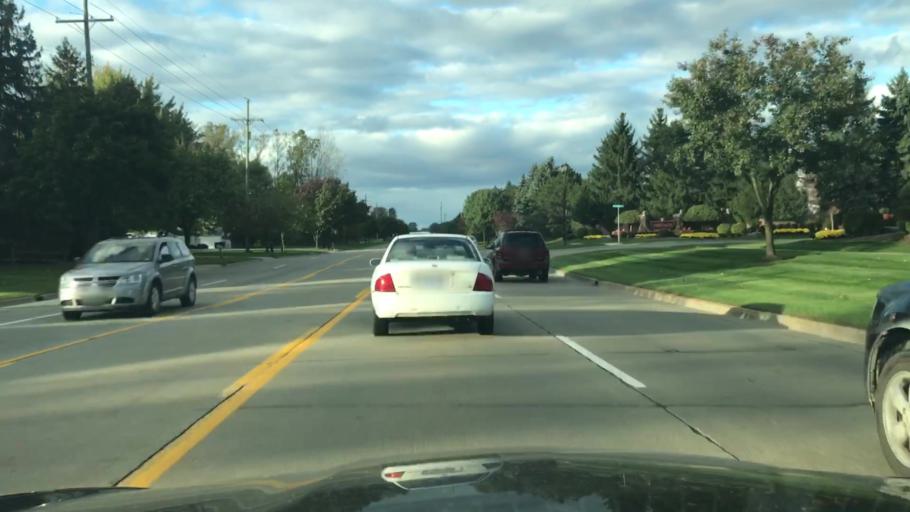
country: US
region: Michigan
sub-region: Macomb County
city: Utica
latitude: 42.6114
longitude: -83.0714
